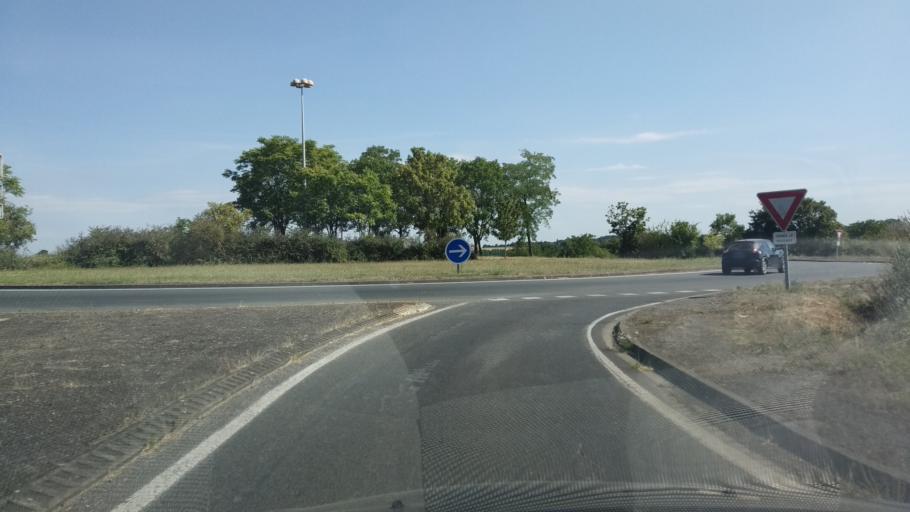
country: FR
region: Poitou-Charentes
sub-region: Departement de la Vienne
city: Cisse
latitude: 46.6299
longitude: 0.2629
